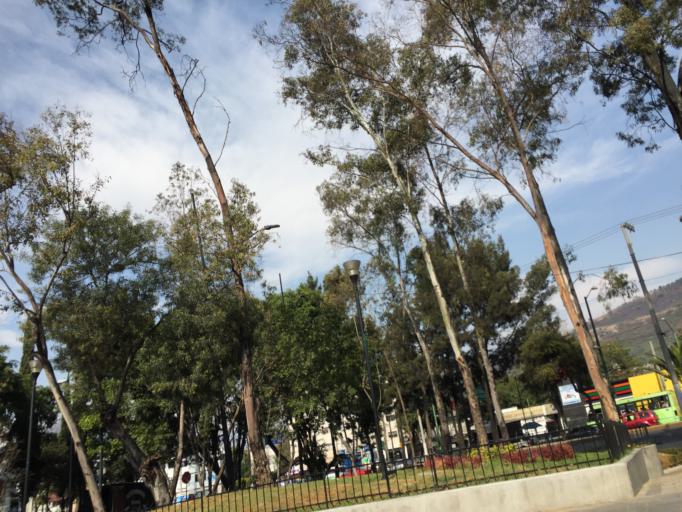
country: MX
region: Mexico
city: Colonia Lindavista
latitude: 19.5012
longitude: -99.1270
